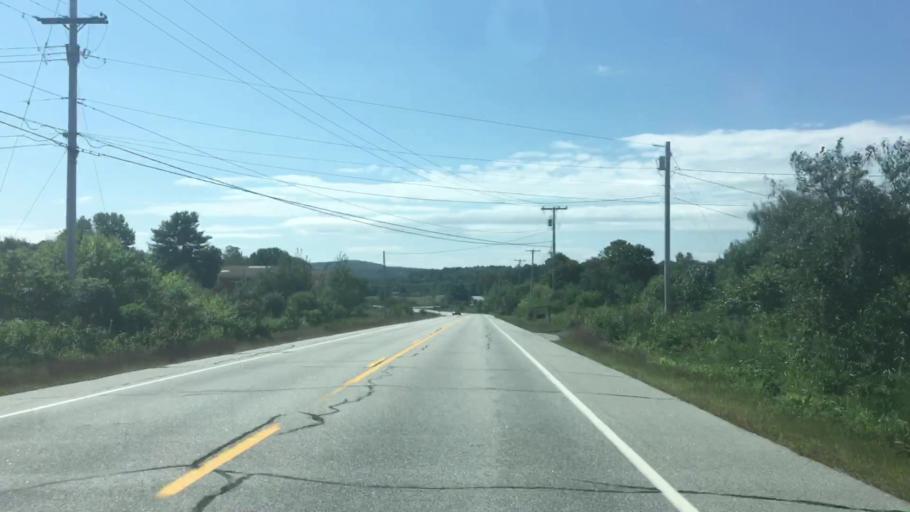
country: US
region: Maine
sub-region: Kennebec County
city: Monmouth
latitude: 44.1665
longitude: -70.0238
